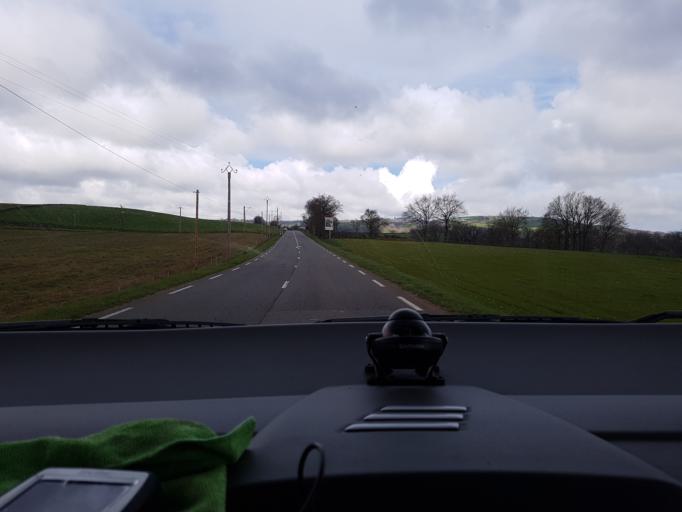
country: FR
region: Midi-Pyrenees
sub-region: Departement de l'Aveyron
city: Moyrazes
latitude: 44.3879
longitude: 2.3991
